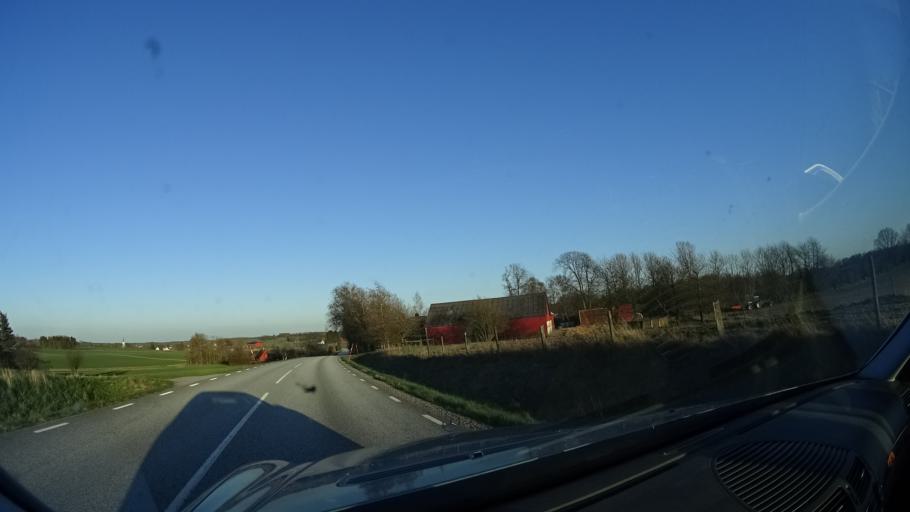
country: SE
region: Skane
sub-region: Klippans Kommun
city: Ljungbyhed
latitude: 55.9643
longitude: 13.2259
